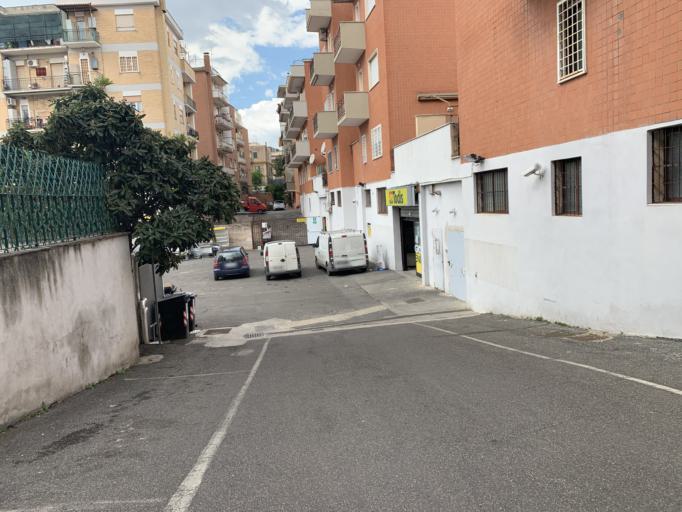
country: VA
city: Vatican City
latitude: 41.8821
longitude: 12.4228
